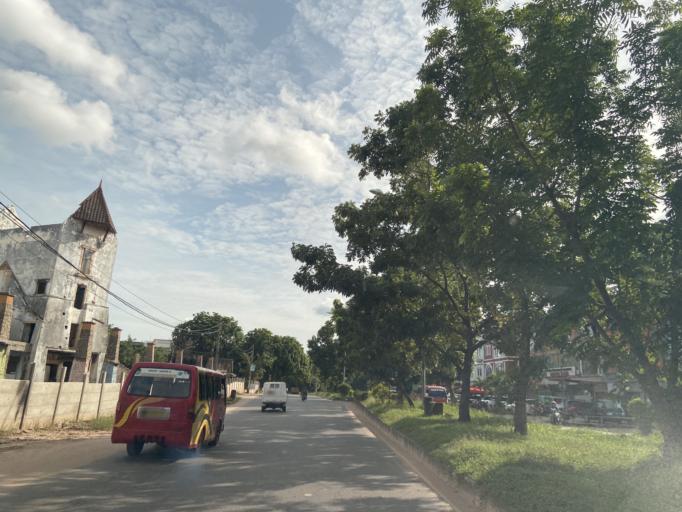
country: SG
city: Singapore
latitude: 1.1470
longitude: 104.0033
